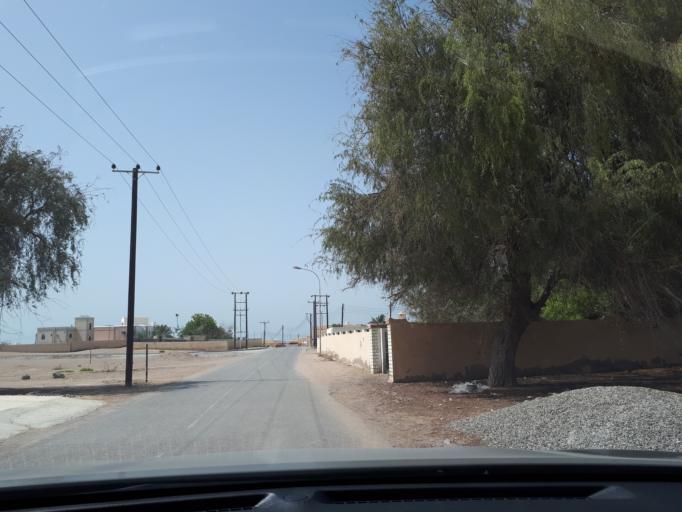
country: OM
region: Al Batinah
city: Barka'
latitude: 23.7049
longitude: 57.9353
